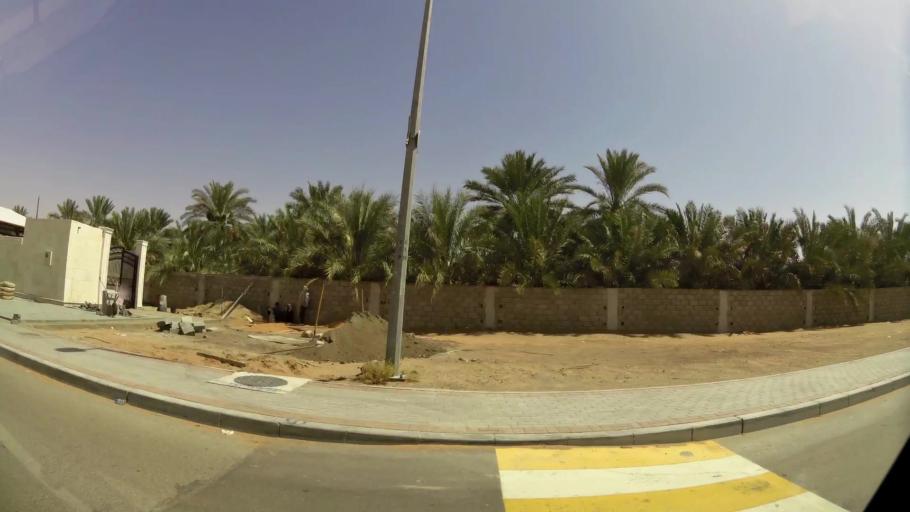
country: OM
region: Al Buraimi
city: Al Buraymi
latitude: 24.2924
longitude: 55.7596
